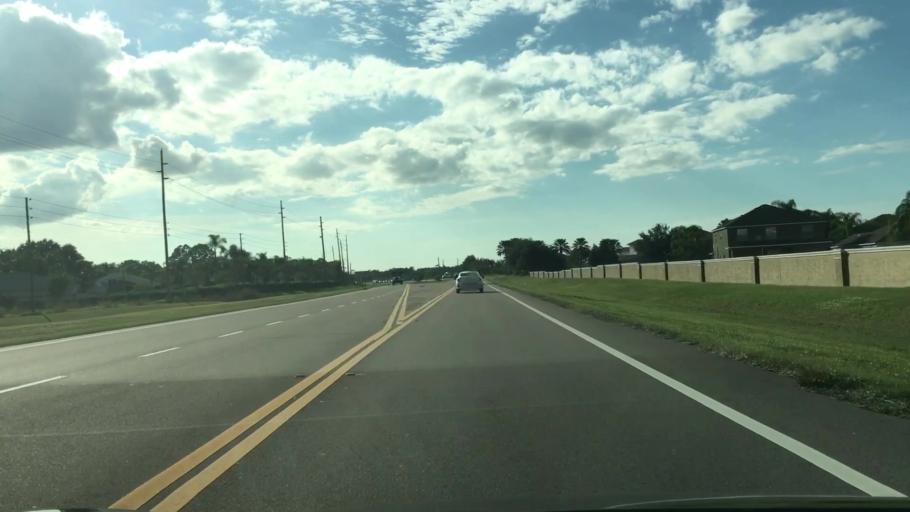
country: US
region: Florida
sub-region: Pasco County
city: Trinity
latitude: 28.1785
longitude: -82.6598
